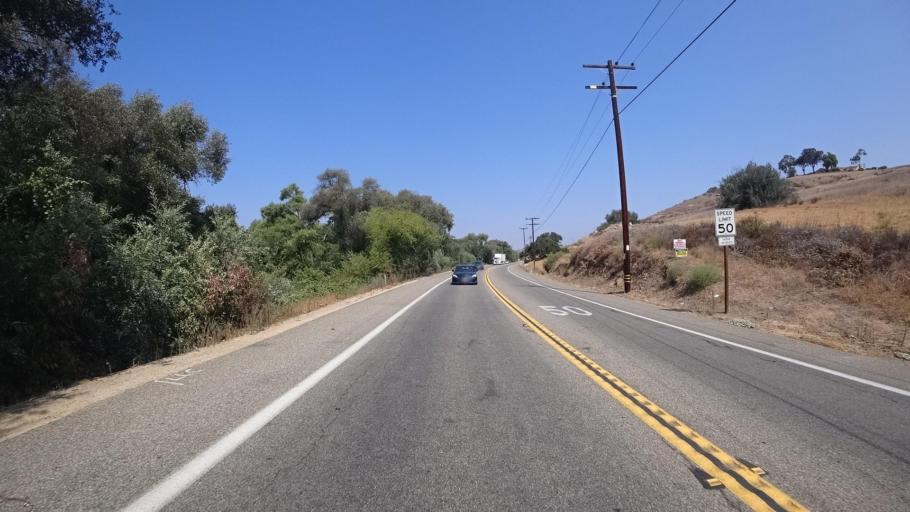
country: US
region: California
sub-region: San Diego County
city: Bonsall
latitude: 33.2977
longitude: -117.2248
